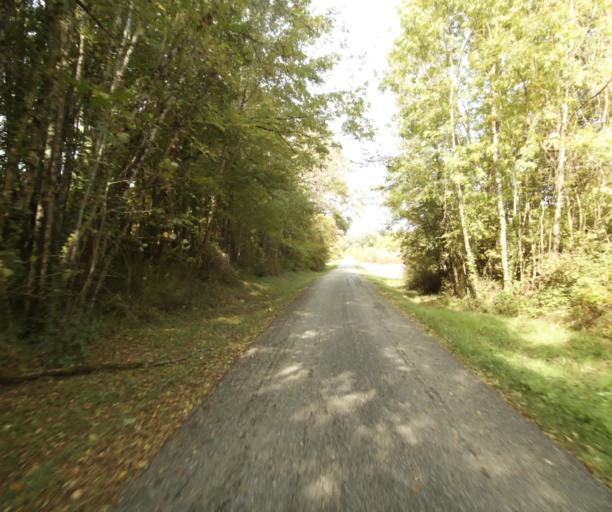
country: FR
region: Midi-Pyrenees
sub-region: Departement du Tarn-et-Garonne
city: Corbarieu
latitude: 43.9618
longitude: 1.3773
